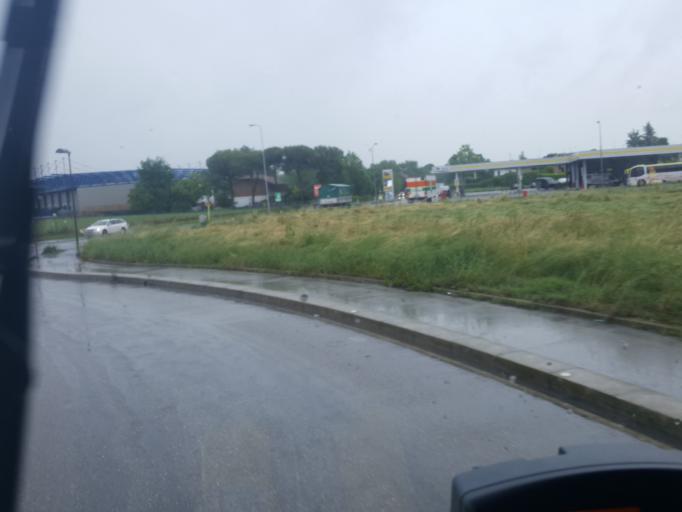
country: IT
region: Emilia-Romagna
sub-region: Forli-Cesena
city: Forli
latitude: 44.2402
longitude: 12.0861
